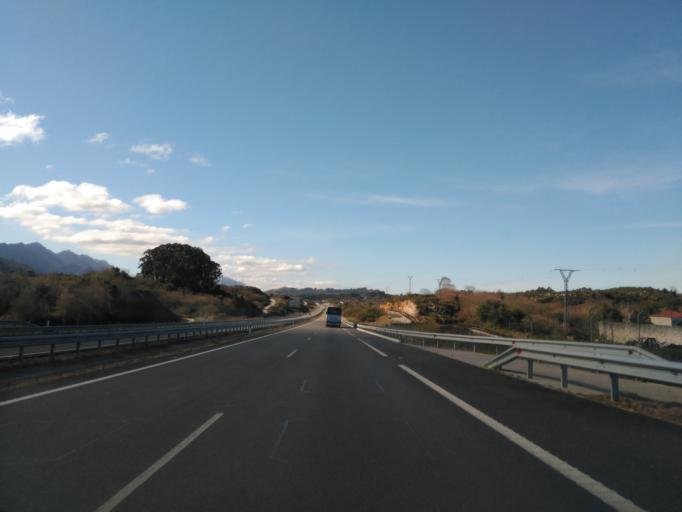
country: ES
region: Asturias
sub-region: Province of Asturias
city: Llanes
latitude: 43.4007
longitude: -4.6675
